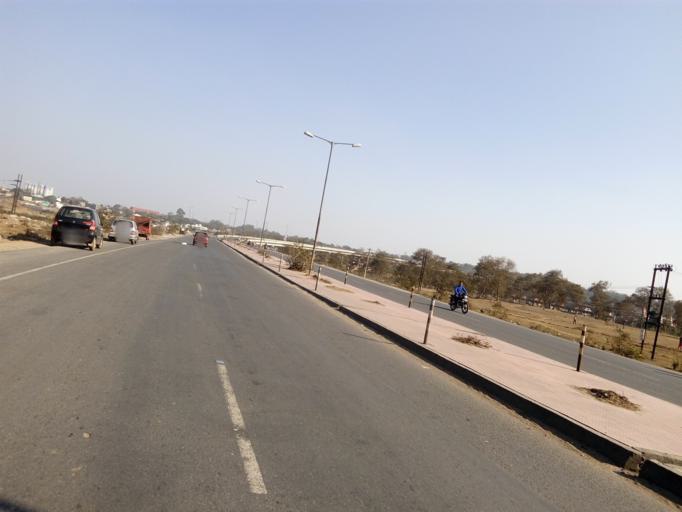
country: IN
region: Jharkhand
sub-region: Ranchi
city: Ranchi
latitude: 23.3552
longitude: 85.3671
